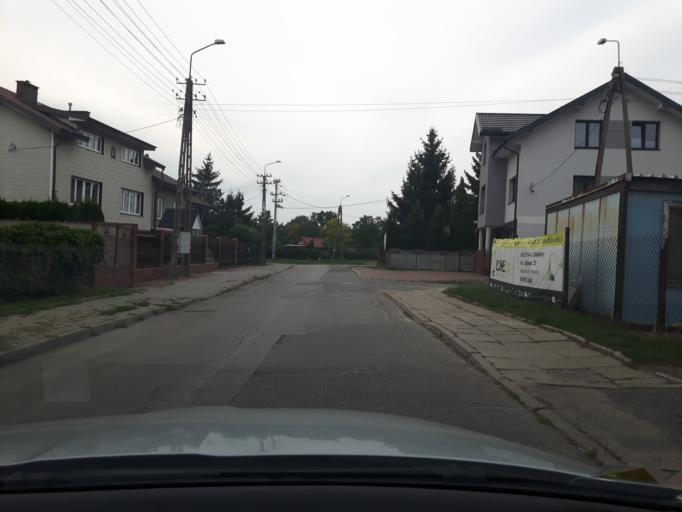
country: PL
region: Masovian Voivodeship
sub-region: Powiat wolominski
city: Zabki
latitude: 52.2907
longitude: 21.0999
